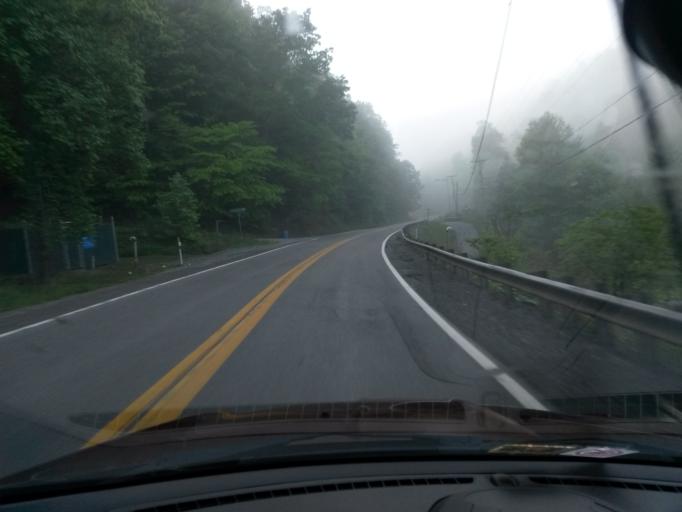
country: US
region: West Virginia
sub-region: McDowell County
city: Welch
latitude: 37.4776
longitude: -81.5441
